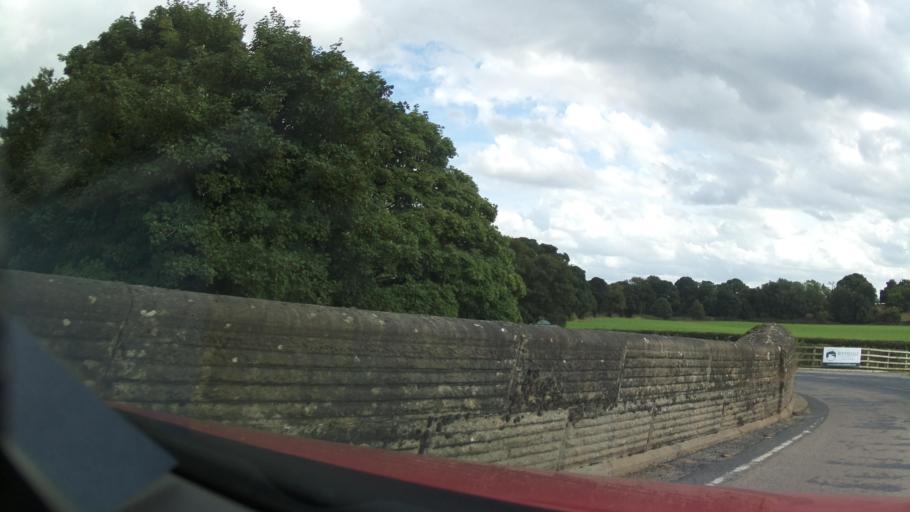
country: GB
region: England
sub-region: North Yorkshire
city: Bedale
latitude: 54.2038
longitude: -1.5880
